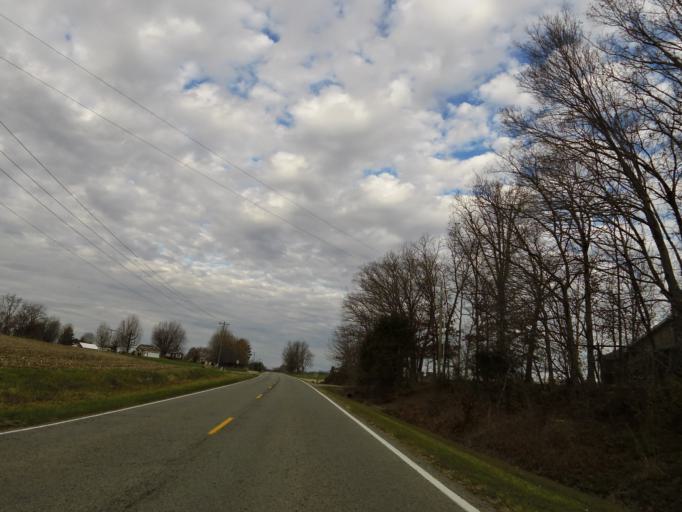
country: US
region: Illinois
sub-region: Jefferson County
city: Mount Vernon
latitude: 38.3585
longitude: -88.9717
